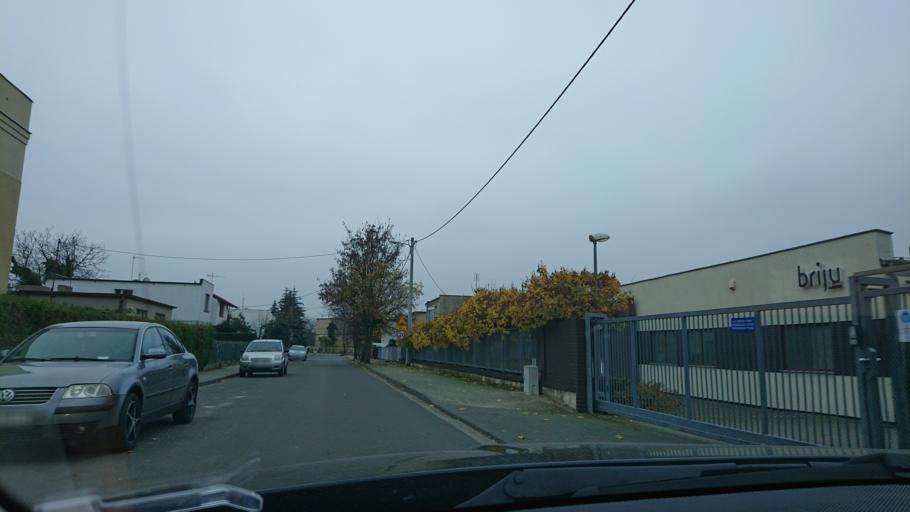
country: PL
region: Greater Poland Voivodeship
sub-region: Powiat gnieznienski
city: Gniezno
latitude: 52.5370
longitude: 17.6242
